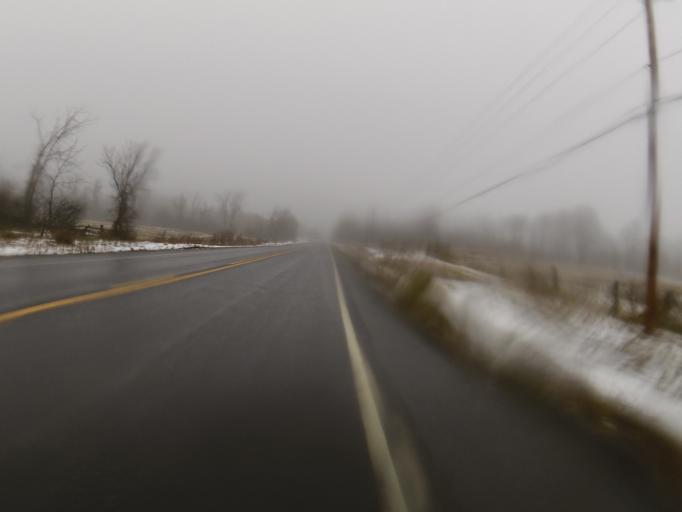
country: CA
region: Ontario
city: Perth
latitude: 44.8172
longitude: -76.3888
